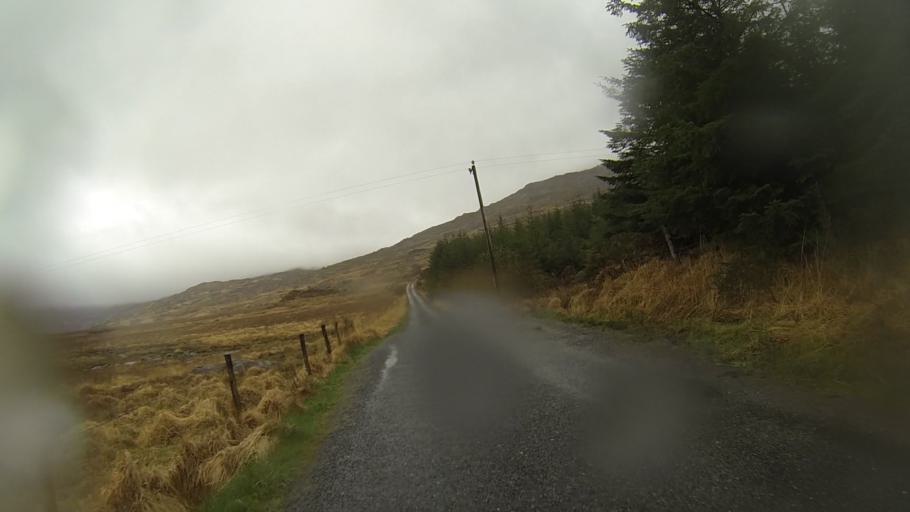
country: IE
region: Munster
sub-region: Ciarrai
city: Kenmare
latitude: 51.9469
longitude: -9.6868
